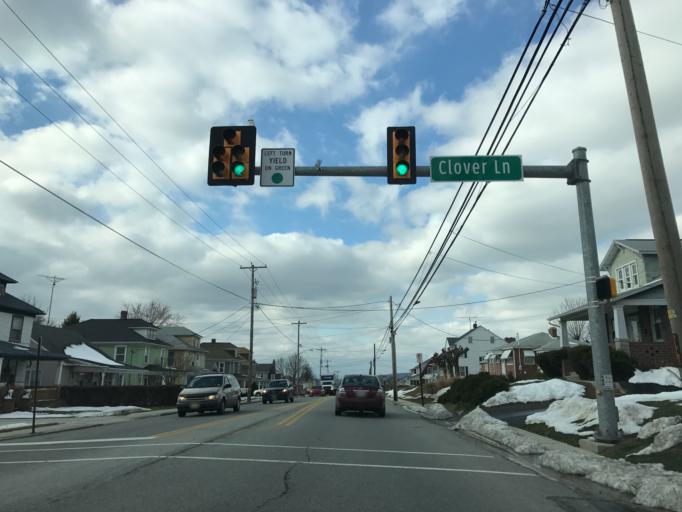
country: US
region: Pennsylvania
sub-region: York County
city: Parkville
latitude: 39.7812
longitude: -76.9633
